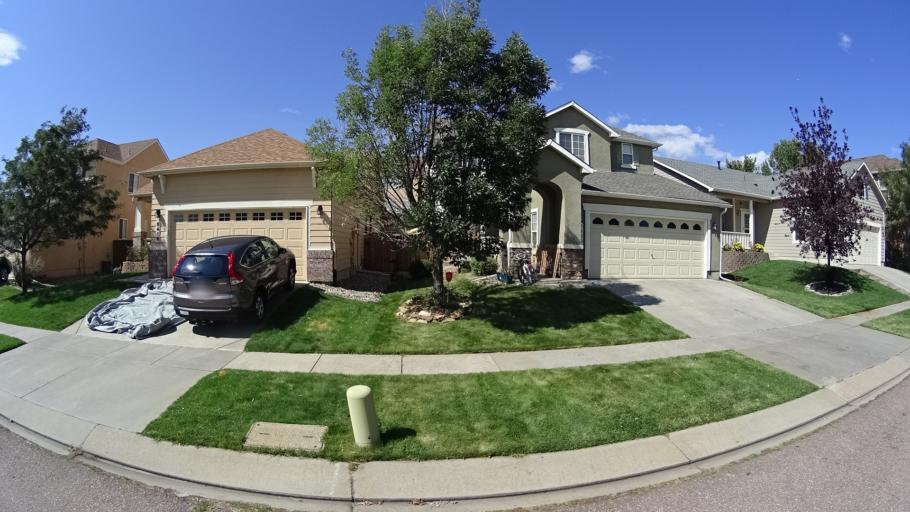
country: US
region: Colorado
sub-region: El Paso County
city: Cimarron Hills
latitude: 38.9190
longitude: -104.7029
